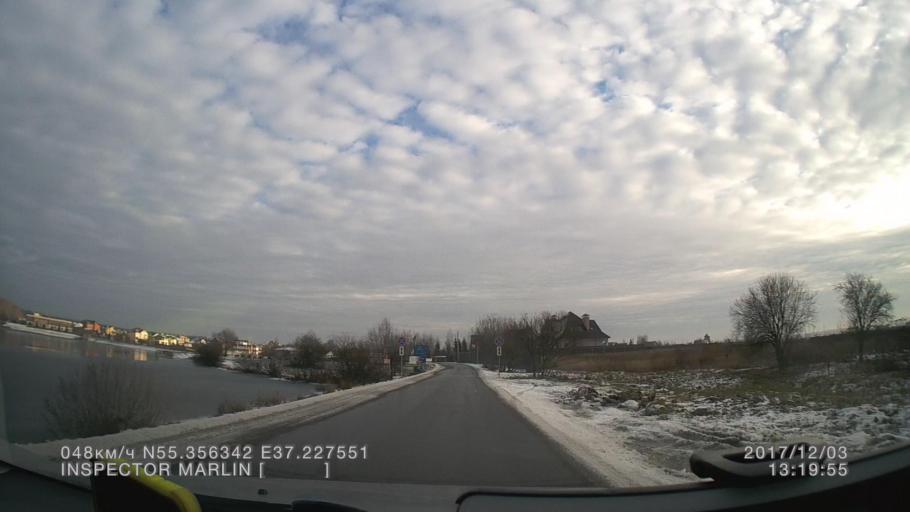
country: RU
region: Moskovskaya
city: Troitsk
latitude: 55.3563
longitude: 37.2276
